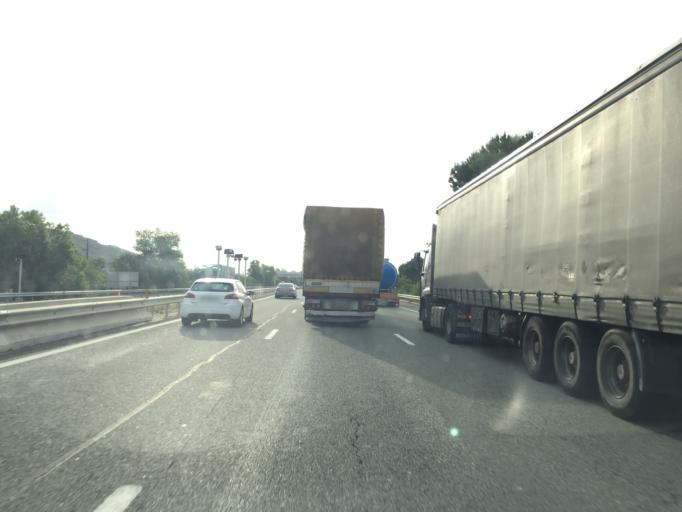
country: FR
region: Provence-Alpes-Cote d'Azur
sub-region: Departement du Var
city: Le Cannet-des-Maures
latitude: 43.4016
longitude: 6.3739
